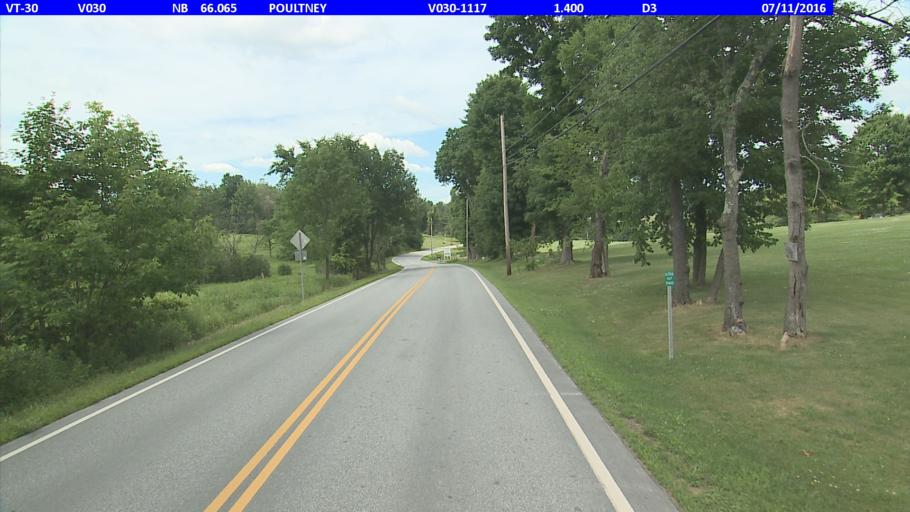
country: US
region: Vermont
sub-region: Rutland County
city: Poultney
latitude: 43.4835
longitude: -73.2027
